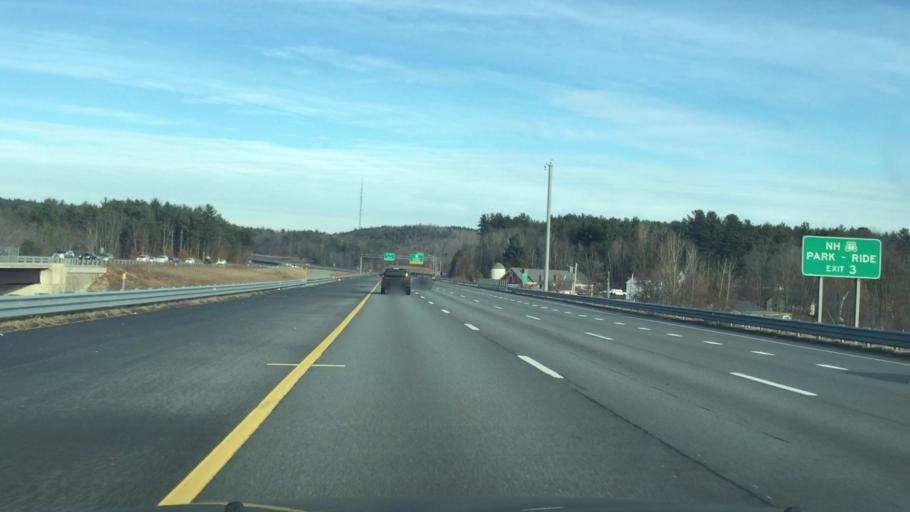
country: US
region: New Hampshire
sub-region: Rockingham County
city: Windham
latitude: 42.7991
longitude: -71.2714
